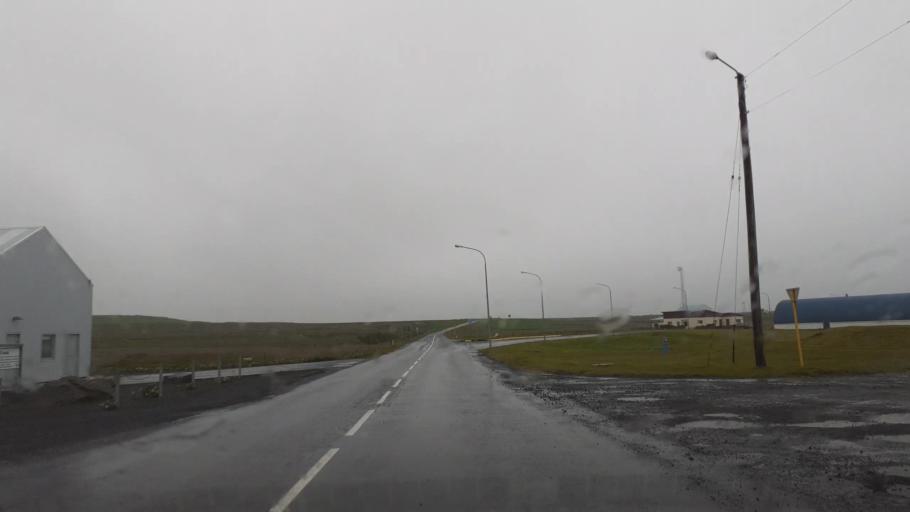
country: IS
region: Northeast
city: Husavik
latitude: 66.4562
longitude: -15.9510
